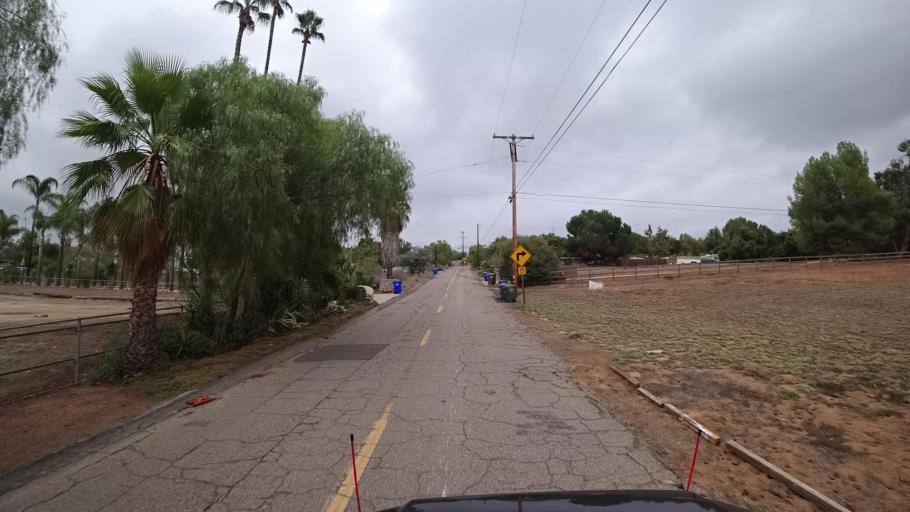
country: US
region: California
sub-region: San Diego County
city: Ramona
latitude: 33.0561
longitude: -116.8841
